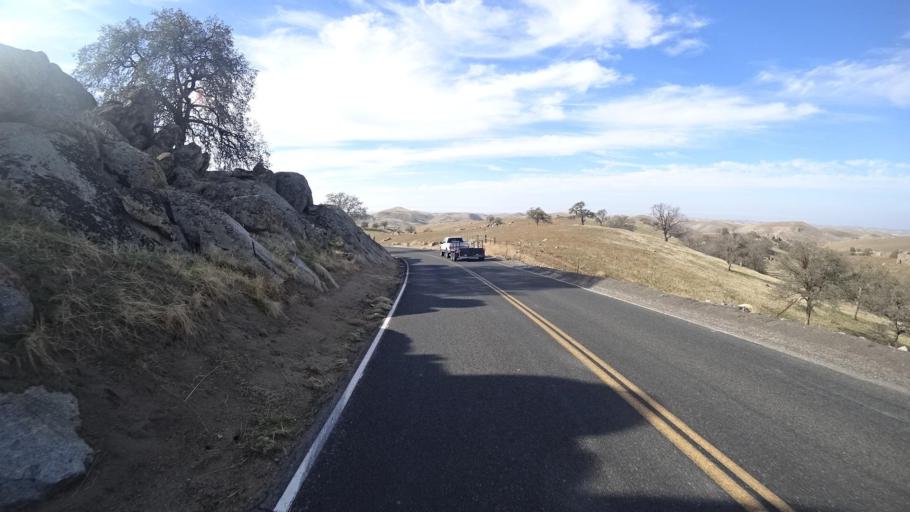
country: US
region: California
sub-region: Kern County
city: Oildale
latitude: 35.6167
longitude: -118.8592
